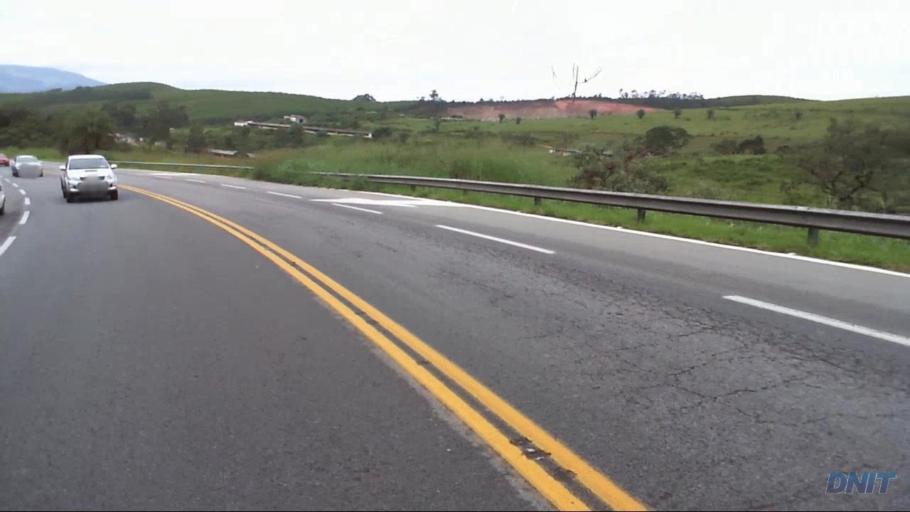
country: BR
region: Minas Gerais
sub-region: Joao Monlevade
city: Joao Monlevade
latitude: -19.8506
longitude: -43.3020
